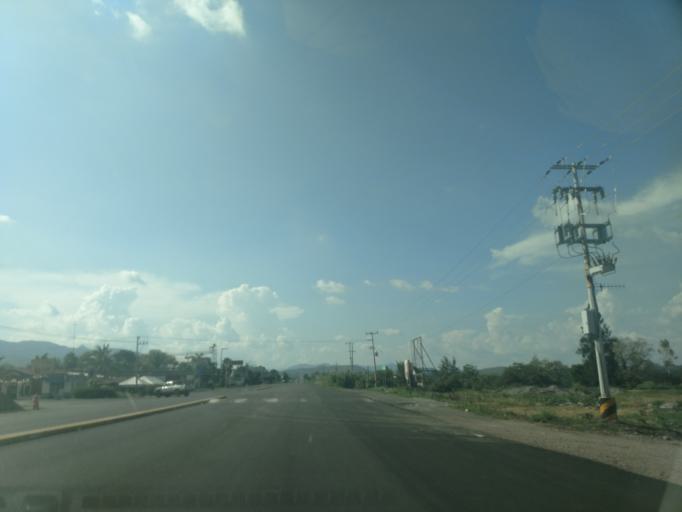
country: MX
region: Jalisco
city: Ahualulco de Mercado
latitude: 20.7075
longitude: -103.9717
